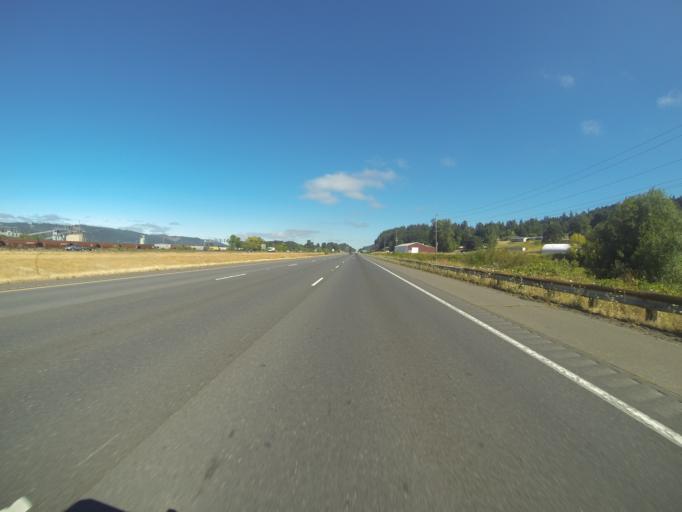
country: US
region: Washington
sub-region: Cowlitz County
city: Kalama
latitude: 46.0273
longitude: -122.8538
